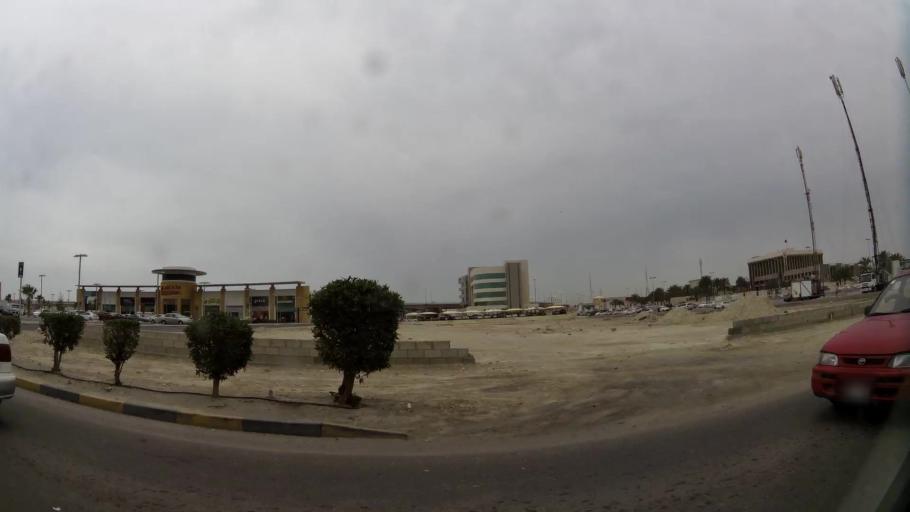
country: BH
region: Northern
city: Madinat `Isa
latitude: 26.1696
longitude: 50.5391
